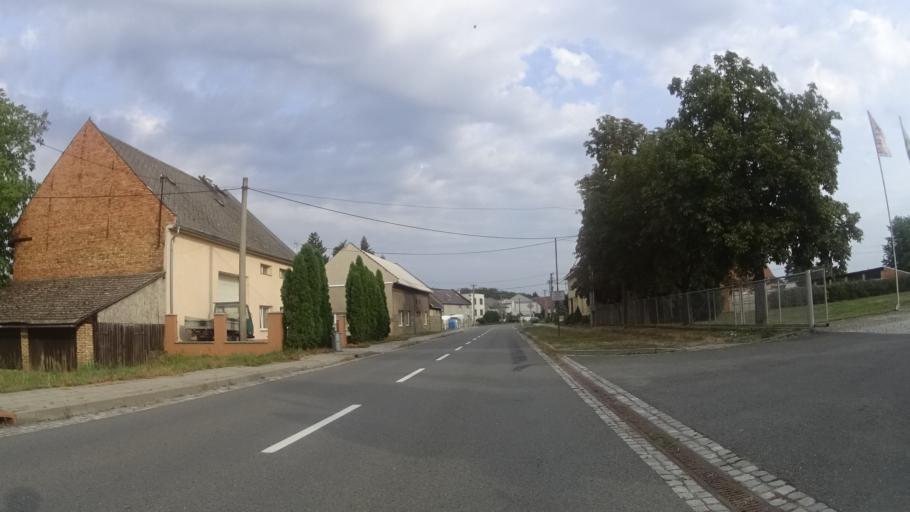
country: CZ
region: Zlin
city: Chropyne
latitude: 49.3370
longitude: 17.3829
